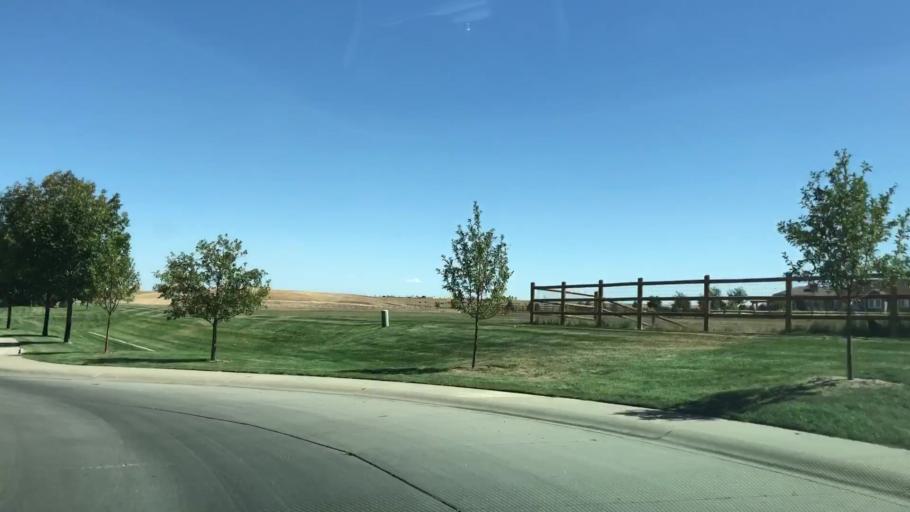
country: US
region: Colorado
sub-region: Weld County
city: Windsor
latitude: 40.4505
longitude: -104.9484
